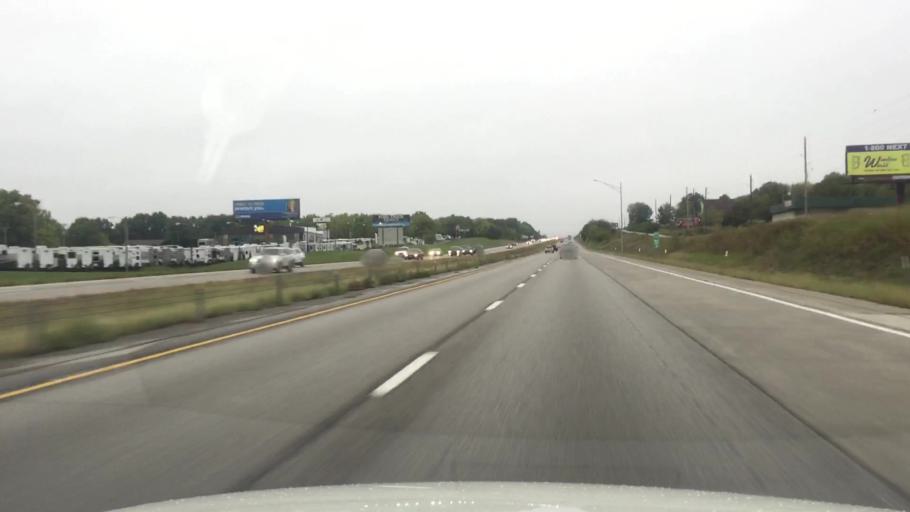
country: US
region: Missouri
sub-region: Jackson County
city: Grain Valley
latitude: 39.0266
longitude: -94.2087
